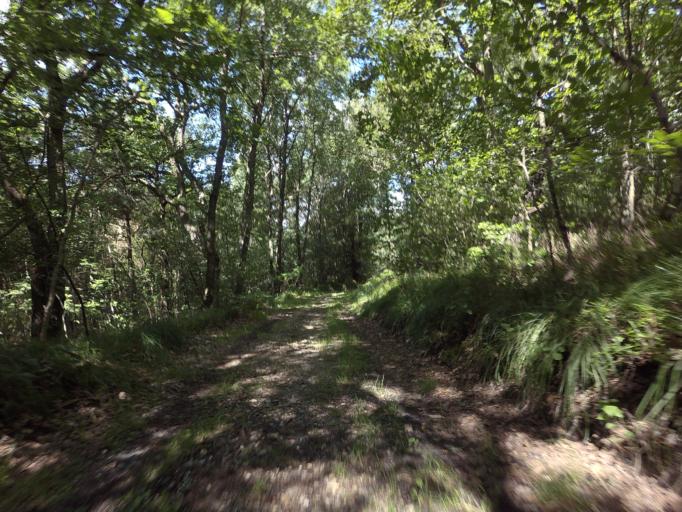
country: DK
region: Central Jutland
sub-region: Silkeborg Kommune
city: Svejbaek
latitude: 56.2154
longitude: 9.6917
